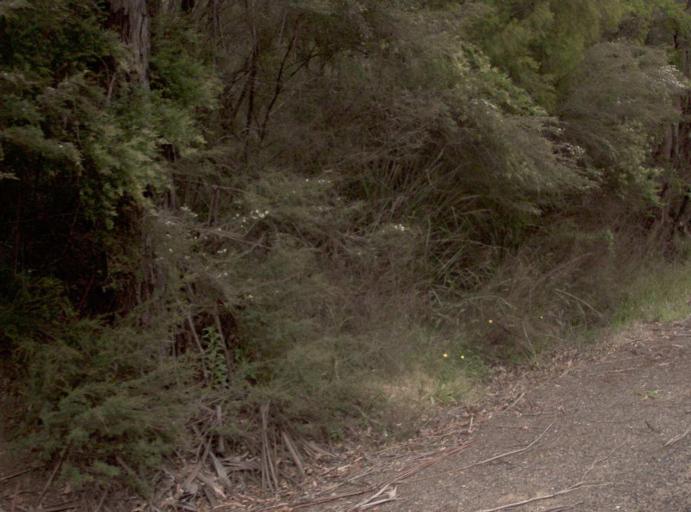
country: AU
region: New South Wales
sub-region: Bombala
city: Bombala
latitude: -37.3988
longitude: 149.1951
